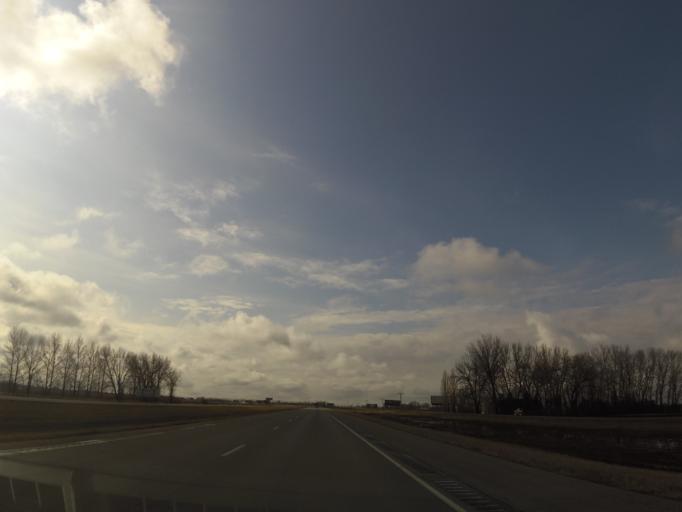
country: US
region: North Dakota
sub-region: Grand Forks County
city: Grand Forks
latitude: 47.8629
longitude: -97.0878
